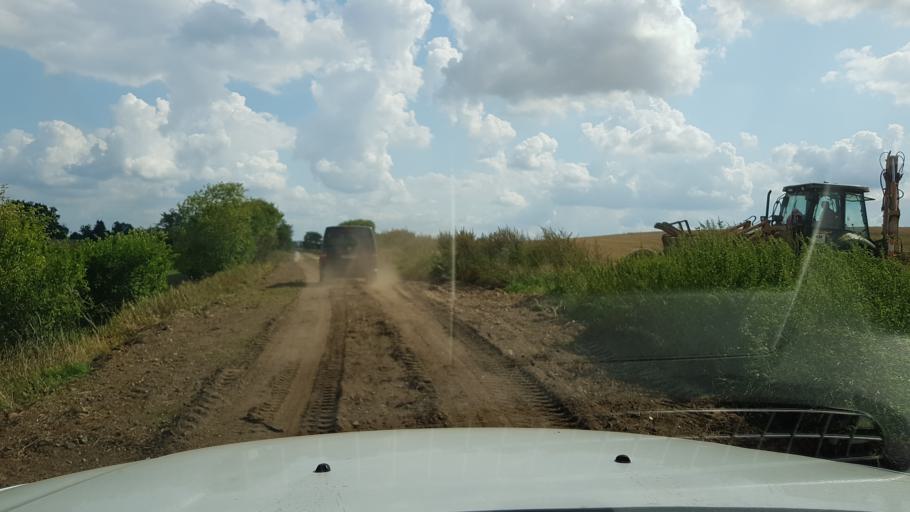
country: PL
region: West Pomeranian Voivodeship
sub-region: Powiat choszczenski
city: Pelczyce
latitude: 53.0775
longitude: 15.3063
